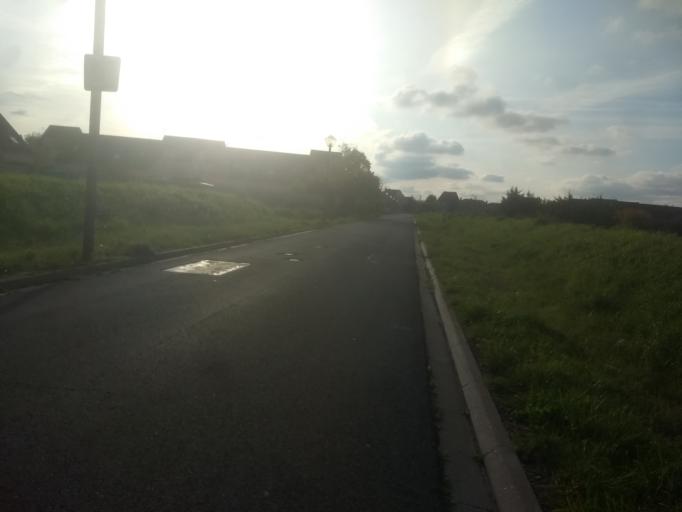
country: FR
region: Nord-Pas-de-Calais
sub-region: Departement du Pas-de-Calais
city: Arras
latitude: 50.2775
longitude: 2.7771
